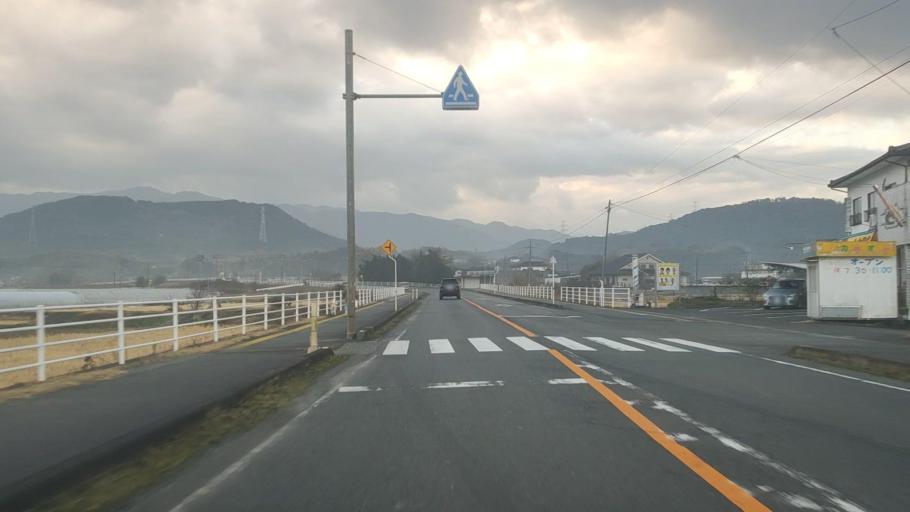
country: JP
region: Kumamoto
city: Matsubase
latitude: 32.6465
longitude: 130.8116
